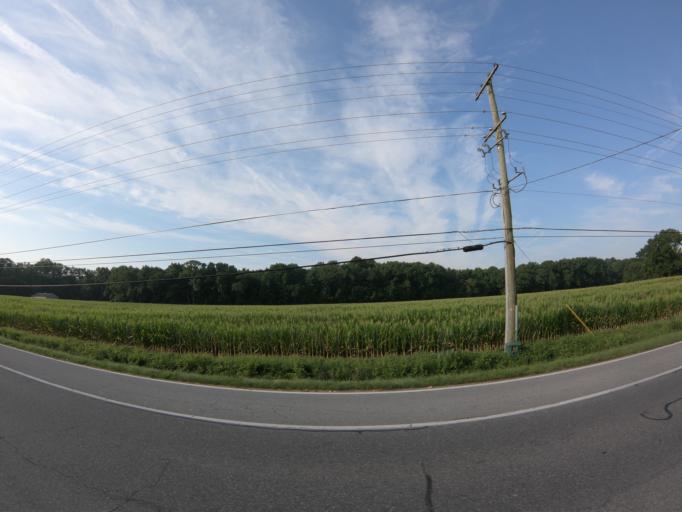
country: US
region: Delaware
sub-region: Sussex County
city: Long Neck
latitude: 38.5560
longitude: -75.1593
